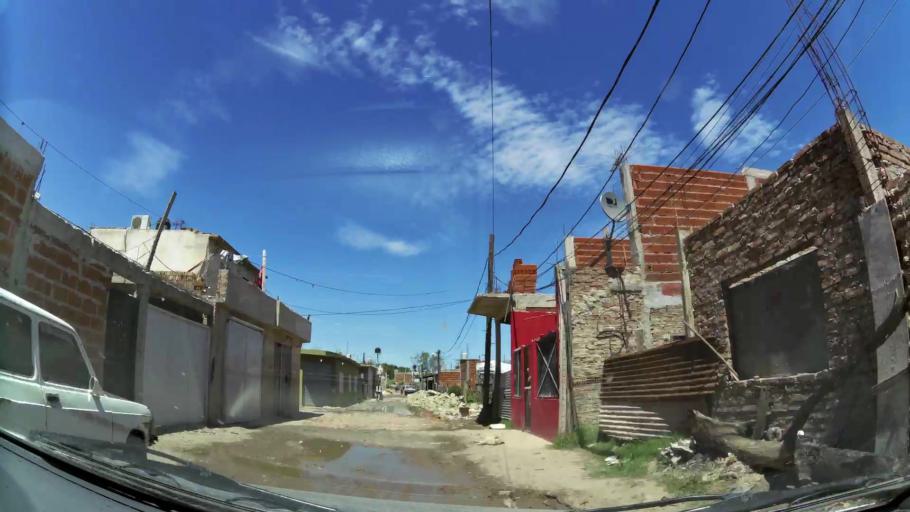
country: AR
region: Buenos Aires
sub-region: Partido de Quilmes
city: Quilmes
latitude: -34.7283
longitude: -58.3172
